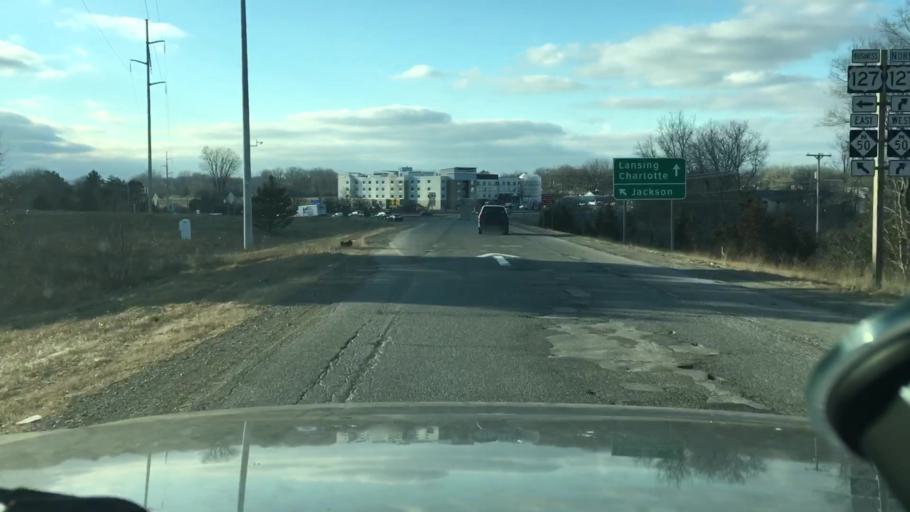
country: US
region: Michigan
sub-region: Jackson County
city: Jackson
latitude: 42.2730
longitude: -84.4248
